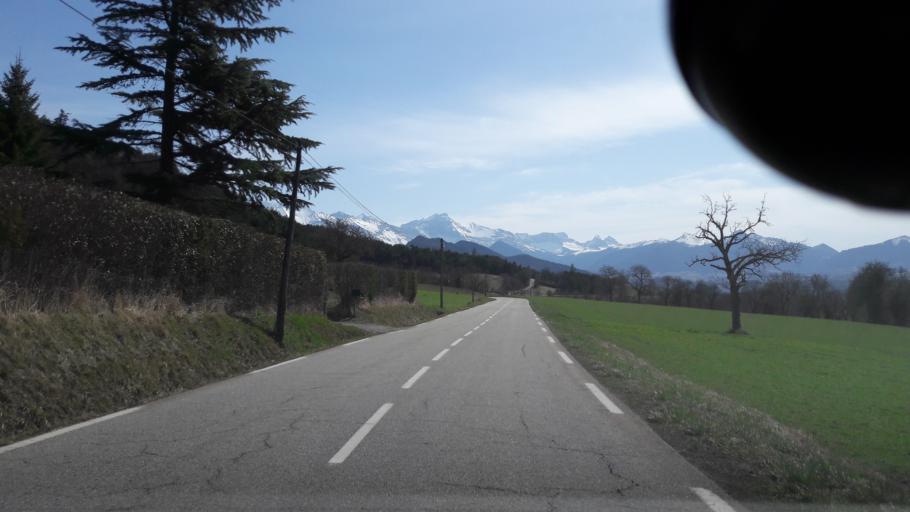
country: FR
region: Rhone-Alpes
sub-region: Departement de l'Isere
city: La Motte-Saint-Martin
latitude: 44.8845
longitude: 5.6454
